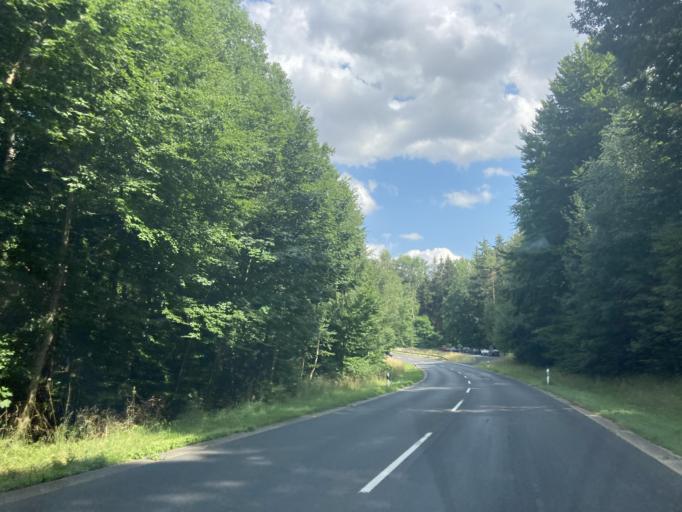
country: DE
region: Hesse
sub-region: Regierungsbezirk Kassel
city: Grossenluder
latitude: 50.5419
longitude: 9.5465
